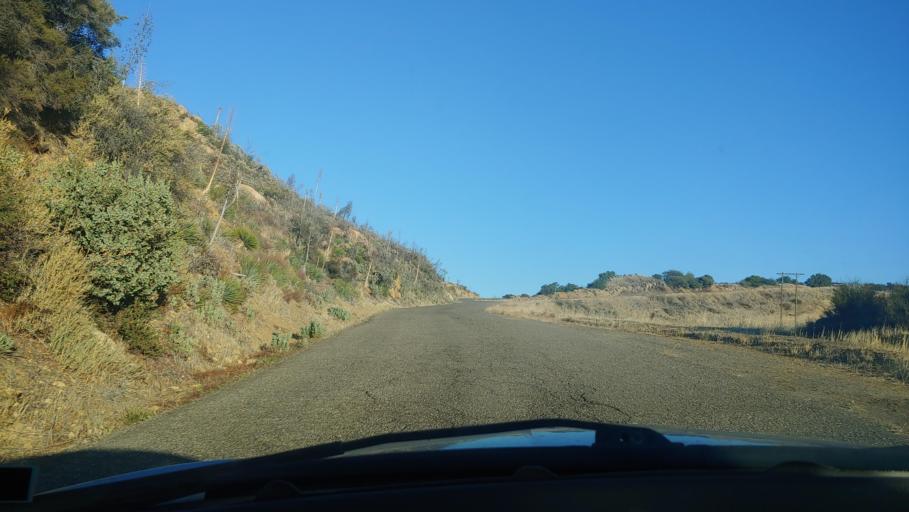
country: US
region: California
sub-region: Santa Barbara County
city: Goleta
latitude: 34.5173
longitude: -119.7818
